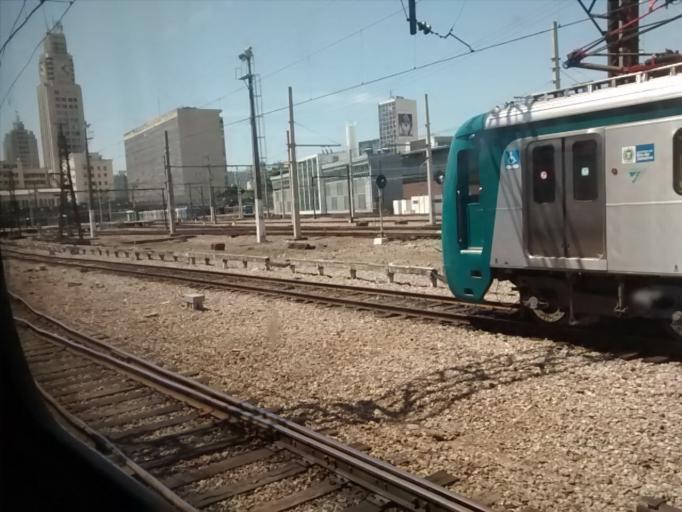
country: BR
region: Rio de Janeiro
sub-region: Rio De Janeiro
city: Rio de Janeiro
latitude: -22.9041
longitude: -43.1957
